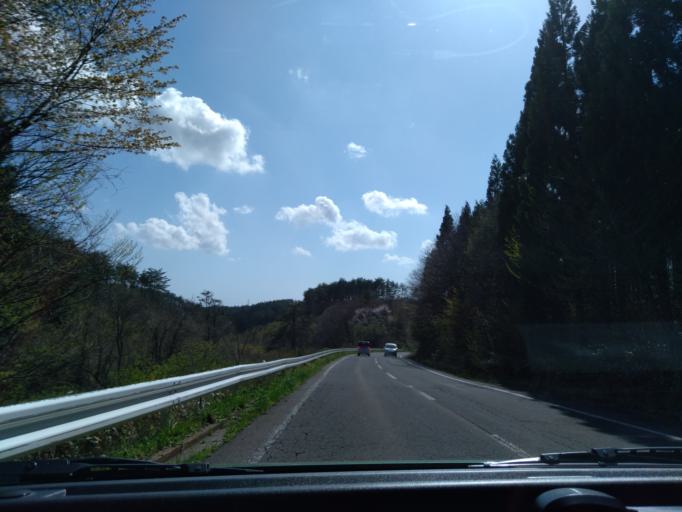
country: JP
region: Akita
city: Akita
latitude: 39.6942
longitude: 140.2478
